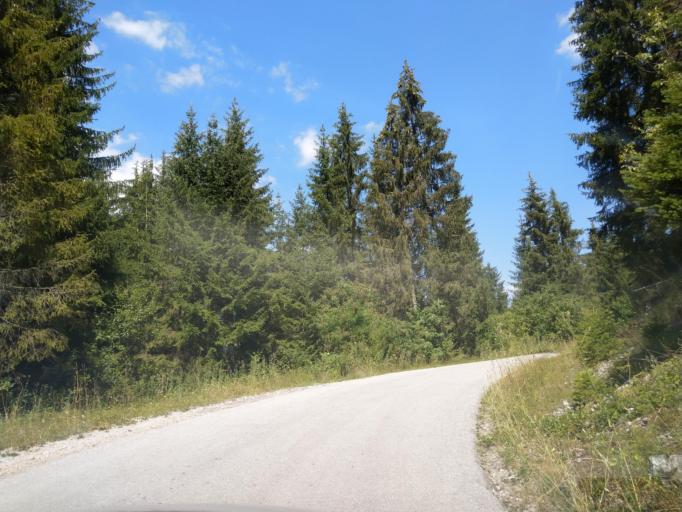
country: RS
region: Central Serbia
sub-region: Zlatiborski Okrug
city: Nova Varos
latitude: 43.4764
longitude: 19.9656
